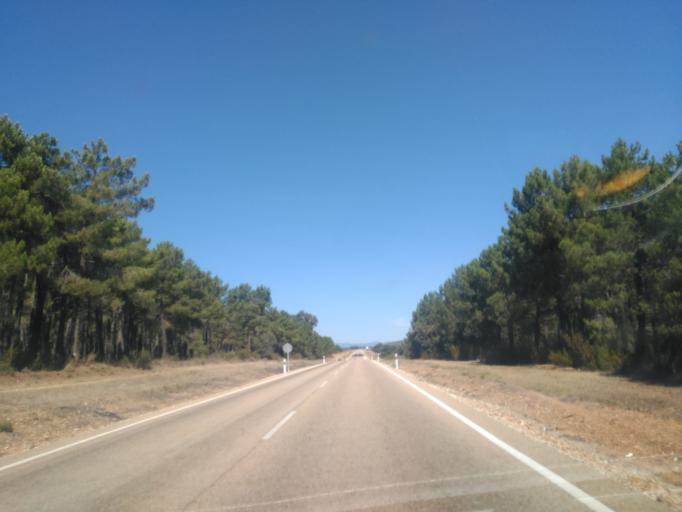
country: ES
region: Castille and Leon
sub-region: Provincia de Zamora
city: Tabara
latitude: 41.8686
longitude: -6.0049
